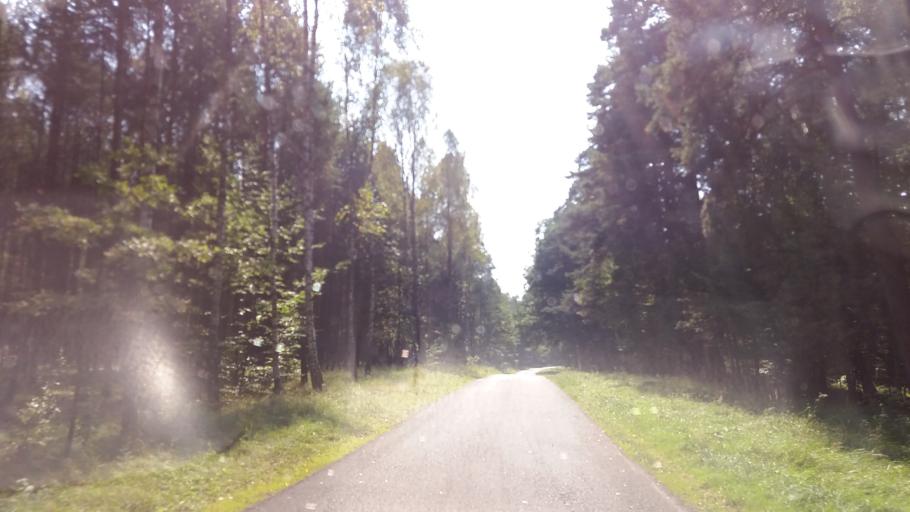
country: PL
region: West Pomeranian Voivodeship
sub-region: Powiat walecki
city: Czlopa
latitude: 53.0859
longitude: 15.9295
